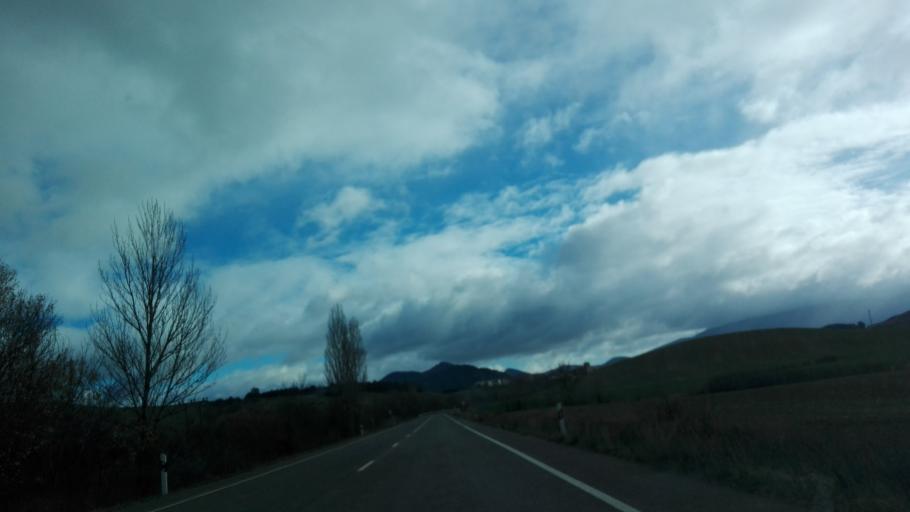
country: ES
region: Navarre
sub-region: Provincia de Navarra
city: Lizoain
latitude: 42.7877
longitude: -1.4690
